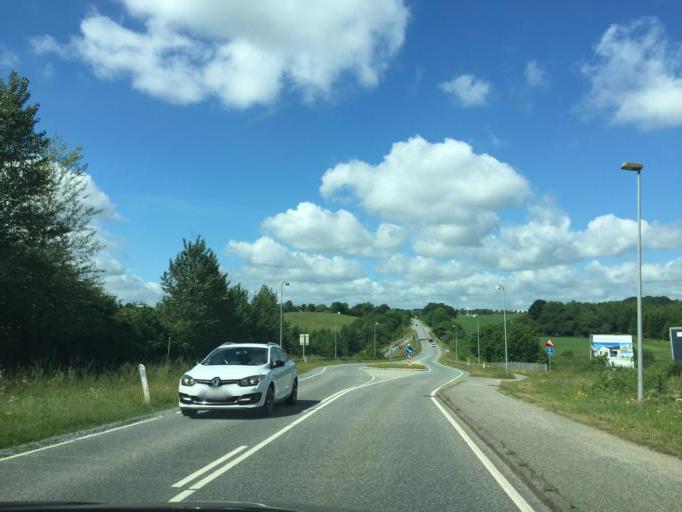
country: DK
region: South Denmark
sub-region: Kolding Kommune
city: Kolding
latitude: 55.5129
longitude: 9.5245
